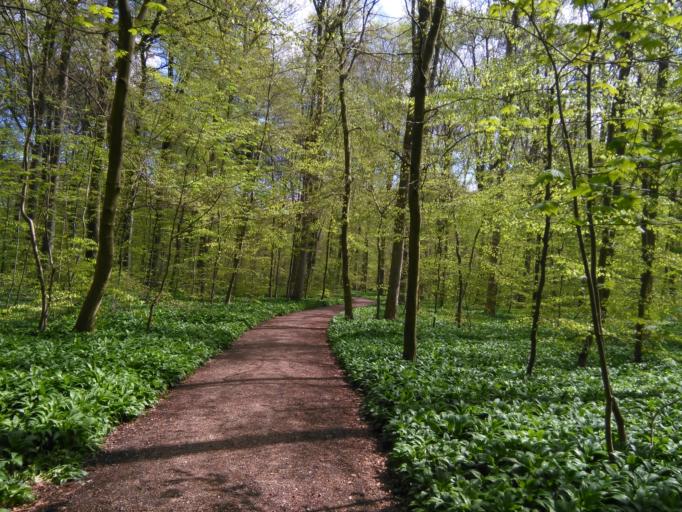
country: DK
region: Central Jutland
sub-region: Arhus Kommune
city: Arhus
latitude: 56.1811
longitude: 10.2276
